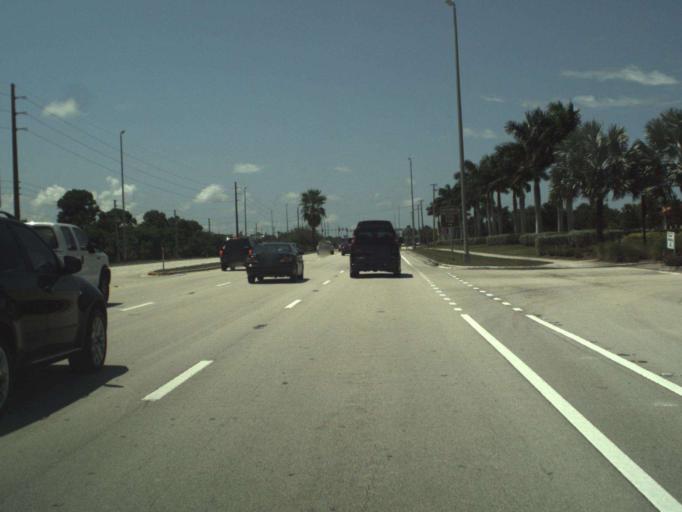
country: US
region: Florida
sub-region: Saint Lucie County
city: Port Saint Lucie
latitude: 27.2952
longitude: -80.3023
